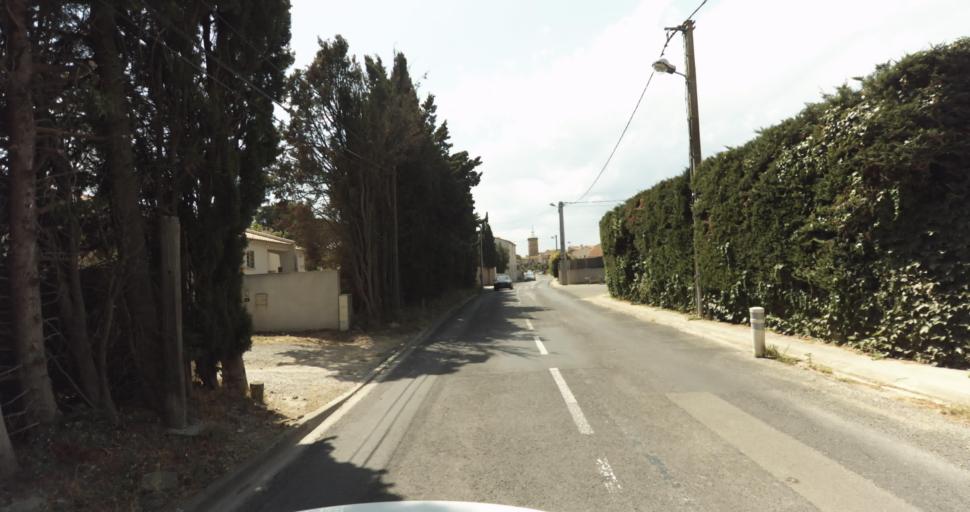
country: FR
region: Languedoc-Roussillon
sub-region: Departement des Pyrenees-Orientales
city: Latour-Bas-Elne
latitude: 42.6051
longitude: 3.0050
